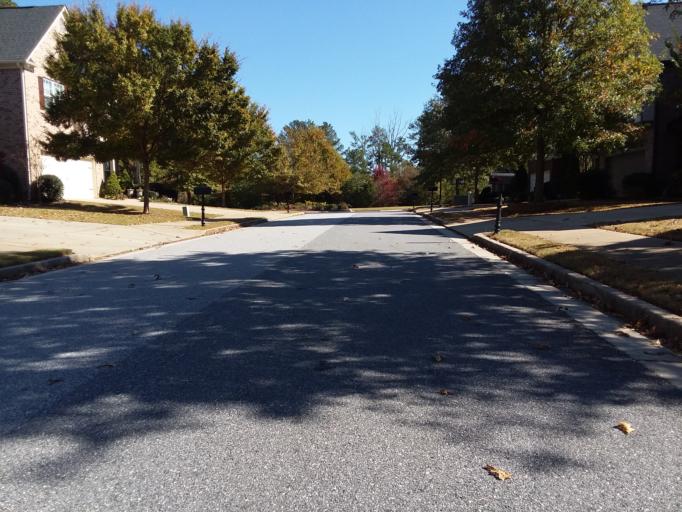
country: US
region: Georgia
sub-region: Fulton County
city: Johns Creek
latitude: 34.0249
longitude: -84.2477
